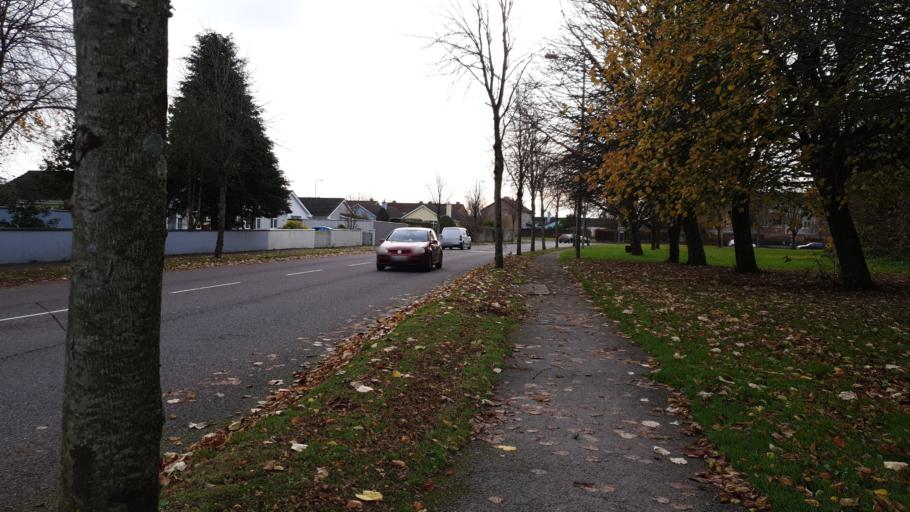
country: IE
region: Munster
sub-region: County Cork
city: Cork
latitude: 51.8918
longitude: -8.4088
